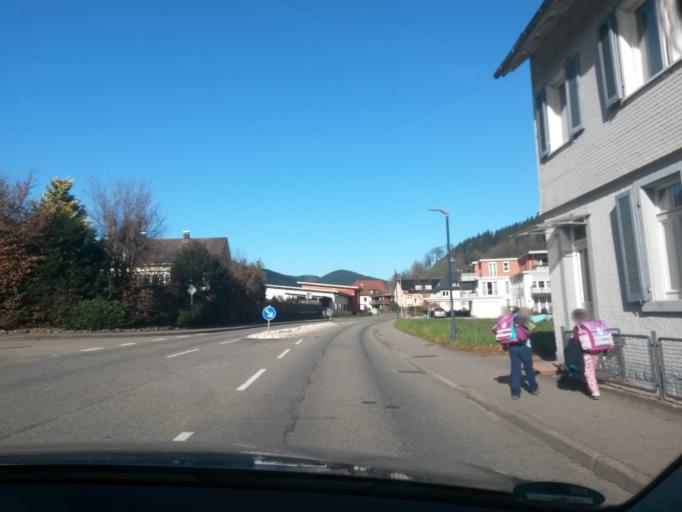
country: DE
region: Baden-Wuerttemberg
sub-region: Freiburg Region
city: Wolfach
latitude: 48.3044
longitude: 8.2205
